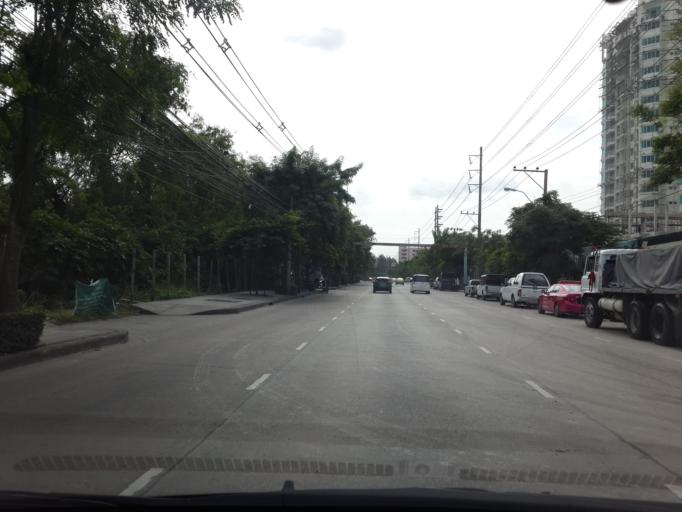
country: TH
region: Bangkok
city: Huai Khwang
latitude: 13.7672
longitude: 100.5788
